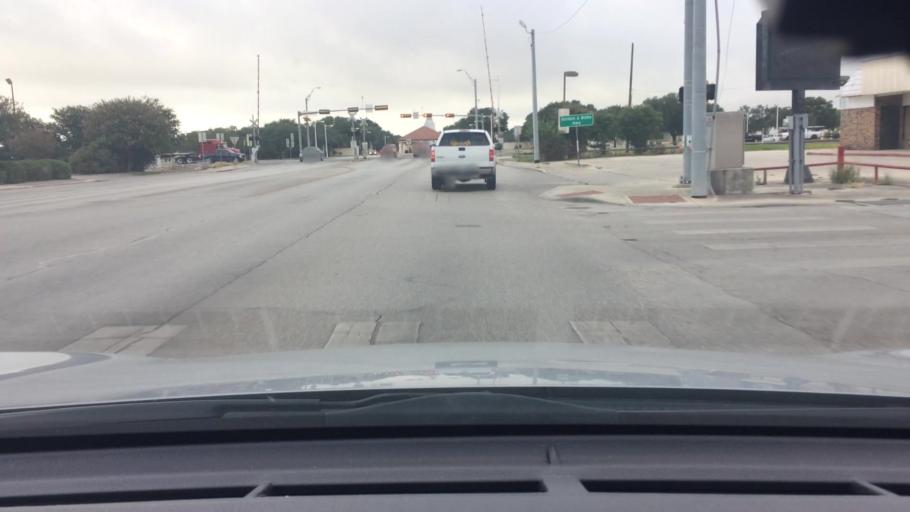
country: US
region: Texas
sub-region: Bexar County
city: Universal City
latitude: 29.5449
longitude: -98.2887
